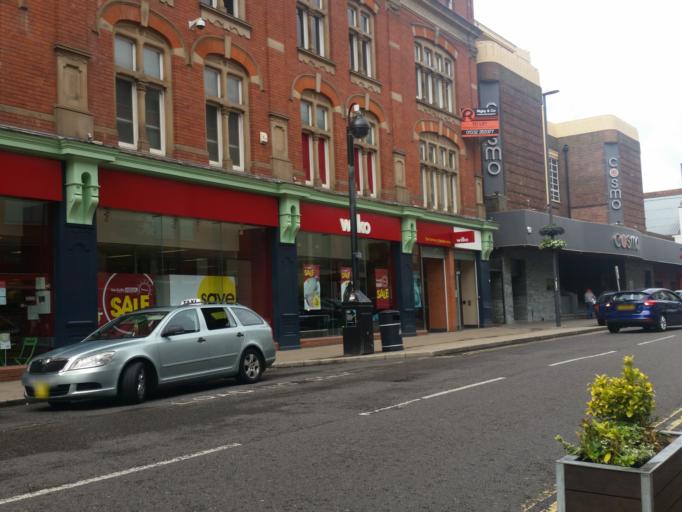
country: GB
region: England
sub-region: Derby
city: Derby
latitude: 52.9186
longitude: -1.4732
